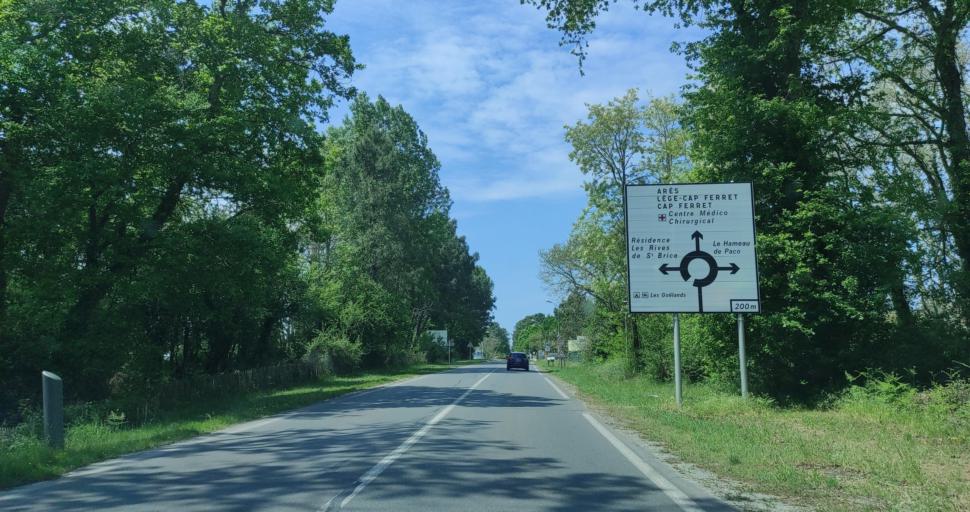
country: FR
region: Aquitaine
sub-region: Departement de la Gironde
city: Andernos-les-Bains
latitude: 44.7569
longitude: -1.1158
